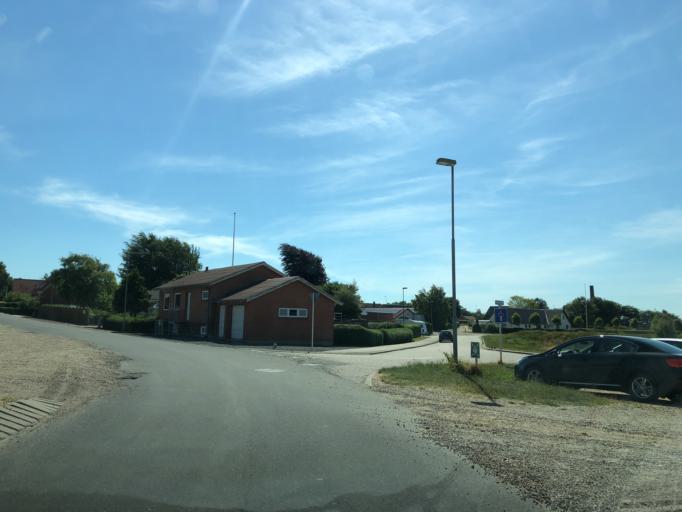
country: DK
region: Central Jutland
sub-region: Holstebro Kommune
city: Vinderup
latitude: 56.4092
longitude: 8.9174
